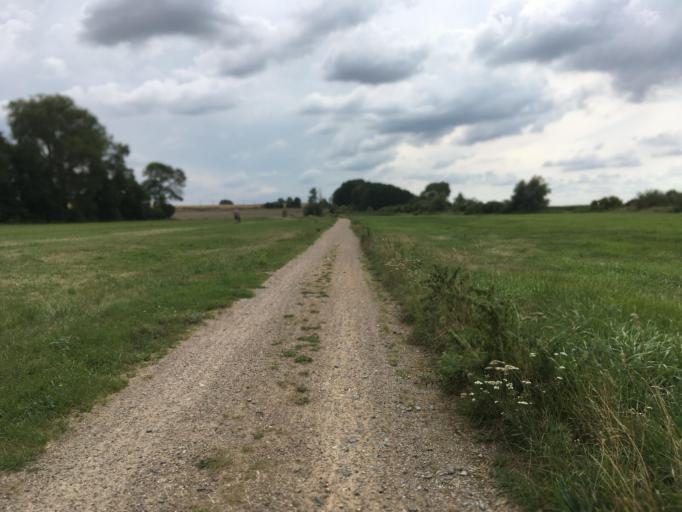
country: DE
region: Brandenburg
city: Prenzlau
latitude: 53.2738
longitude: 13.8821
